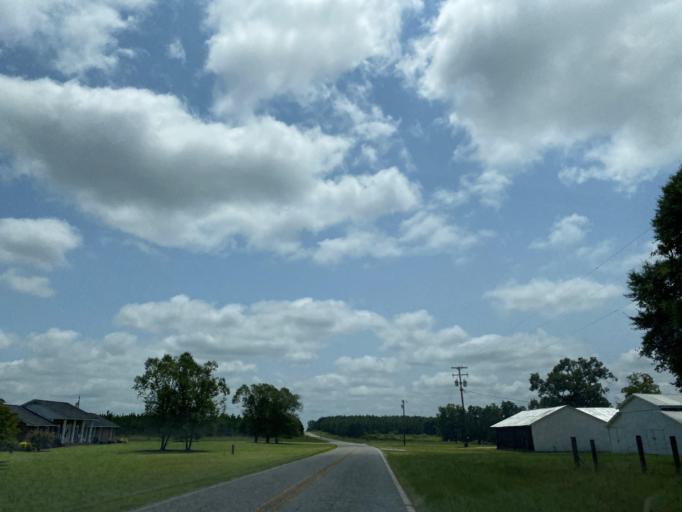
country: US
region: Georgia
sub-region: Wheeler County
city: Alamo
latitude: 32.0693
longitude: -82.7304
